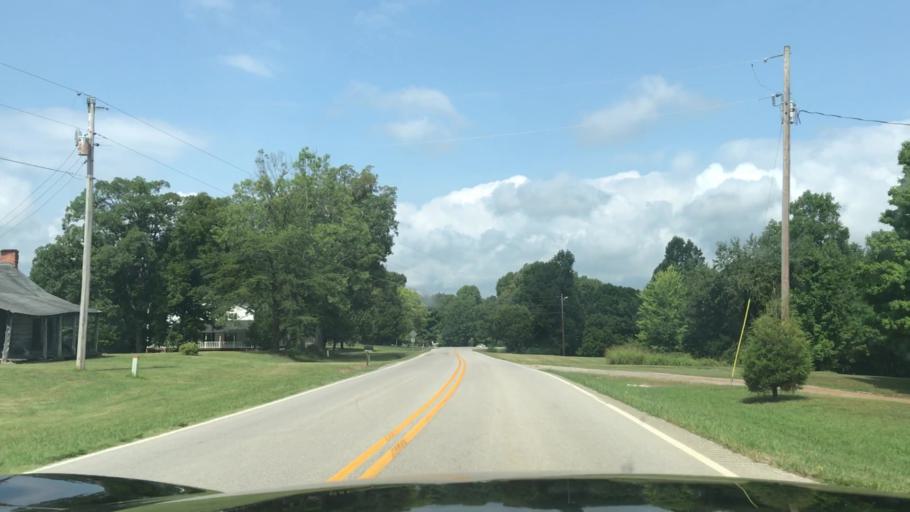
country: US
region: Kentucky
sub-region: Butler County
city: Morgantown
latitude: 37.1822
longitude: -86.8685
